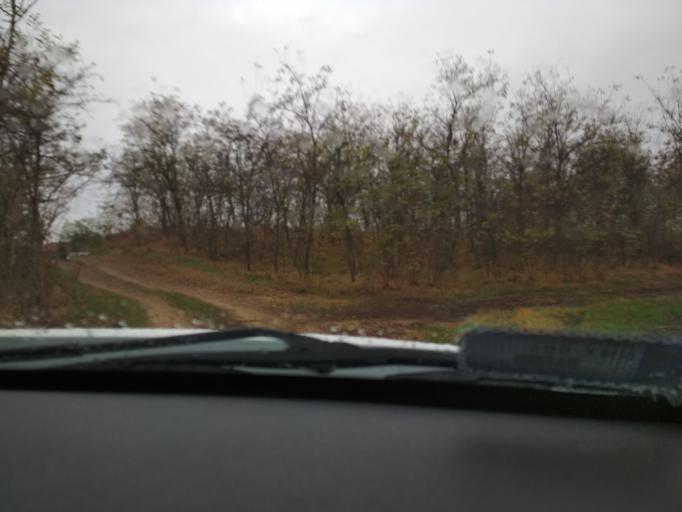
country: HU
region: Csongrad
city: Opusztaszer
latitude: 46.4368
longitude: 20.1334
